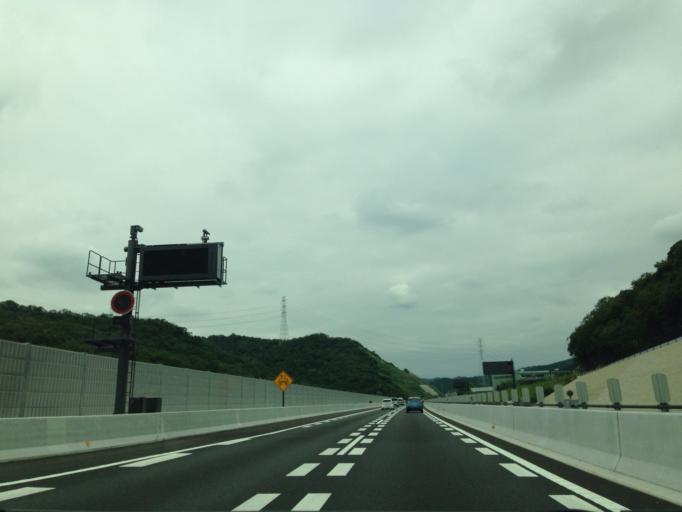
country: JP
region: Aichi
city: Gamagori
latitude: 34.9230
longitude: 137.2724
